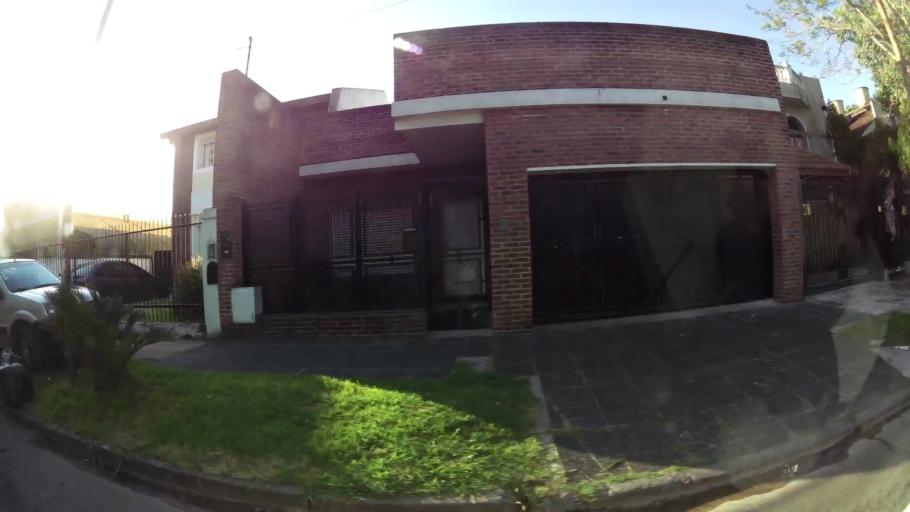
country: AR
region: Buenos Aires
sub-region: Partido de General San Martin
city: General San Martin
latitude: -34.5523
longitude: -58.5476
